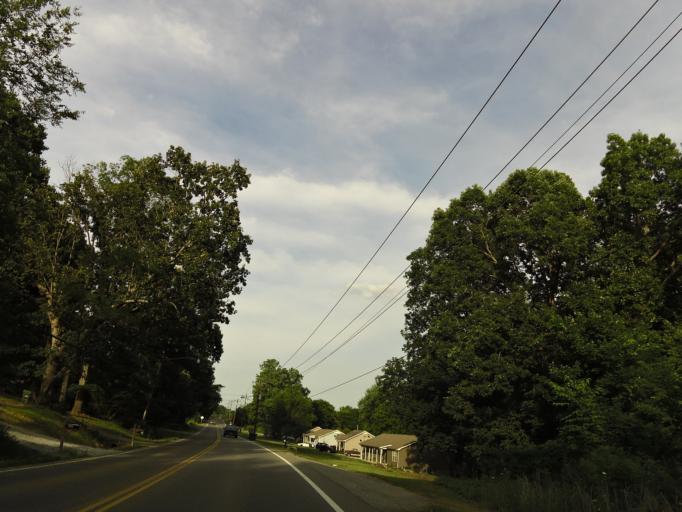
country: US
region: Tennessee
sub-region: Dickson County
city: Dickson
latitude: 36.0642
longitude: -87.3704
